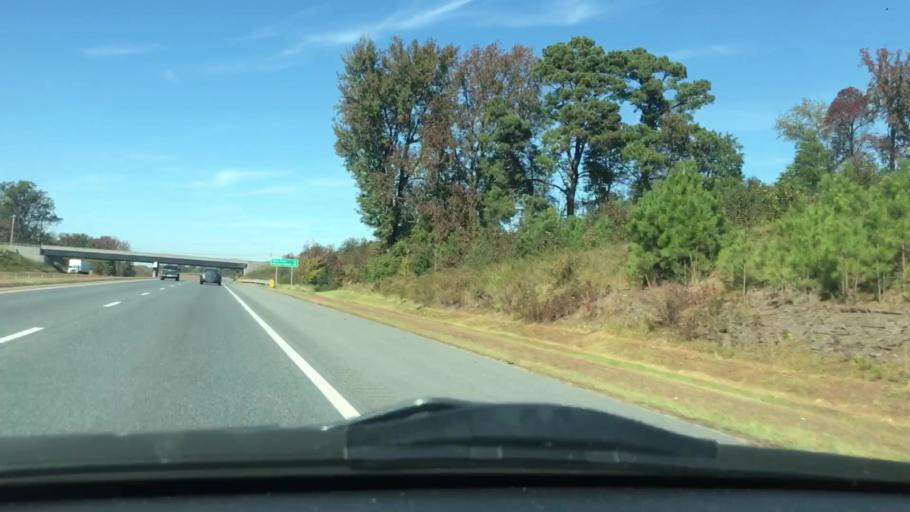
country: US
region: North Carolina
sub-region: Randolph County
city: Randleman
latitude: 35.8330
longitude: -79.8596
